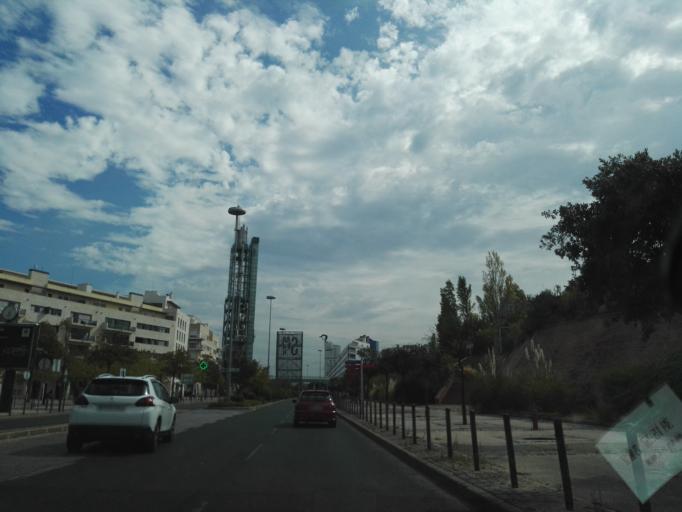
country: PT
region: Lisbon
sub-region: Loures
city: Moscavide
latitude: 38.7610
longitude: -9.0964
